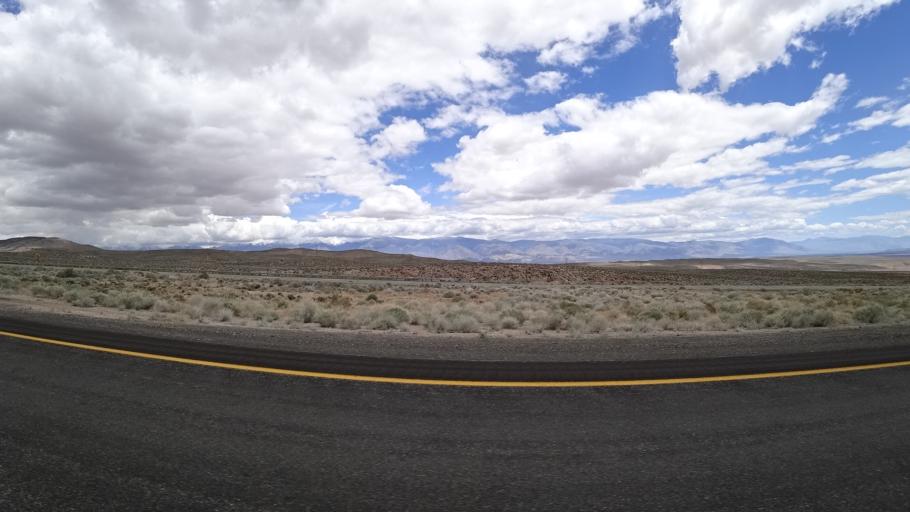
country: US
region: California
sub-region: Inyo County
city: West Bishop
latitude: 37.5052
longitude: -118.5836
